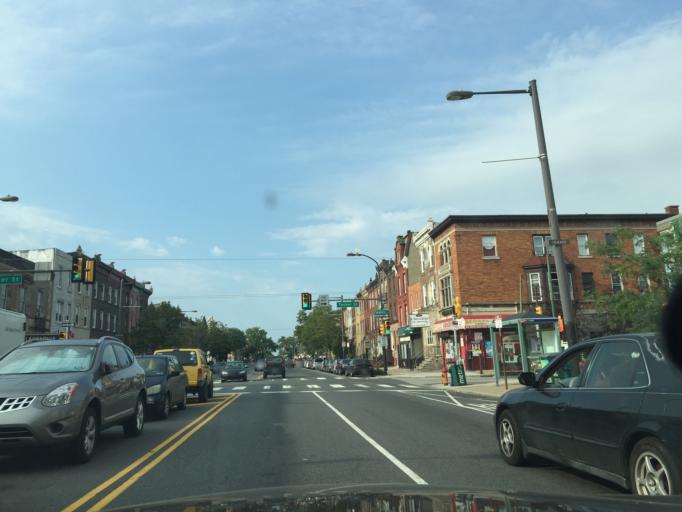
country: US
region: Pennsylvania
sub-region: Philadelphia County
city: Philadelphia
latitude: 39.9309
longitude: -75.1683
